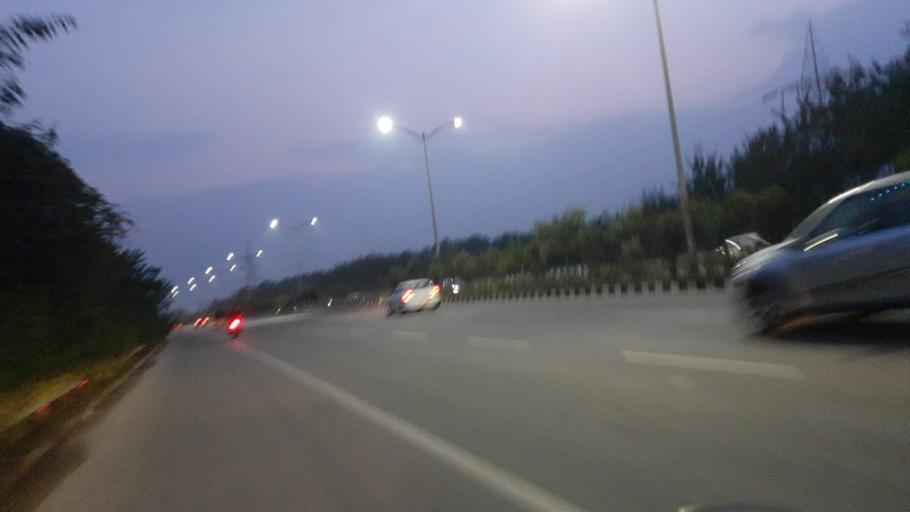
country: IN
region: Telangana
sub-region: Rangareddi
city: Kukatpalli
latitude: 17.4334
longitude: 78.3605
